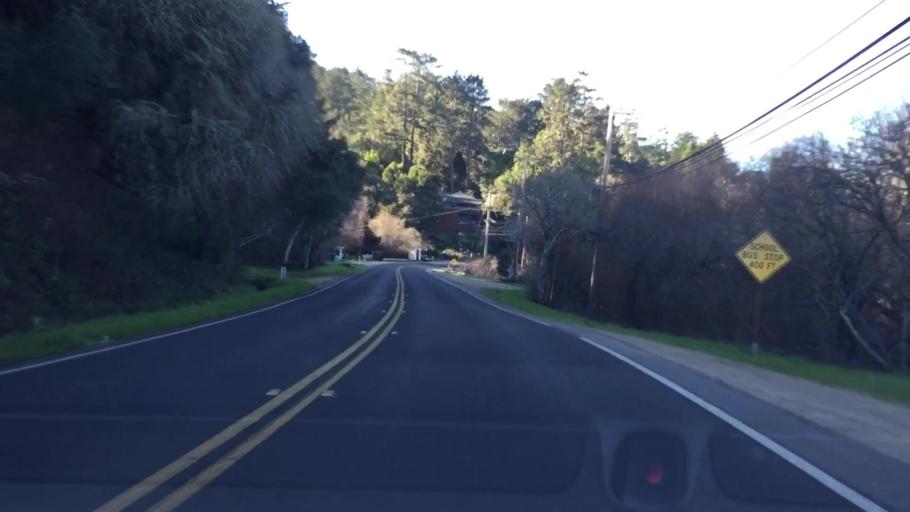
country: US
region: California
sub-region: Marin County
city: Inverness
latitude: 38.0624
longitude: -122.8189
